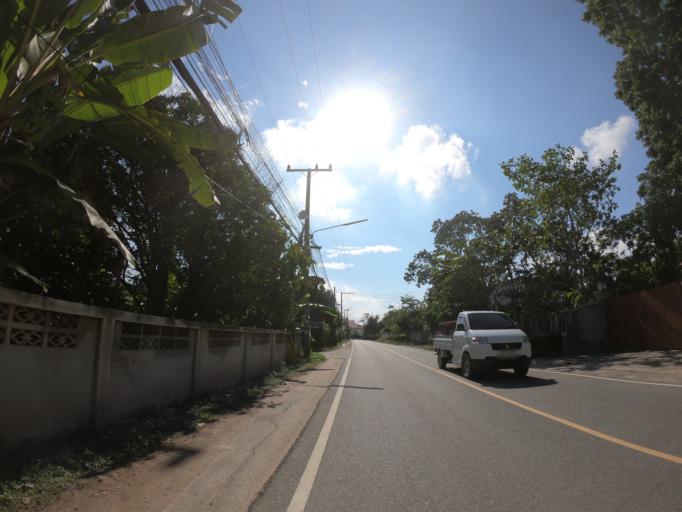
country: TH
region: Chiang Mai
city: San Sai
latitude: 18.8390
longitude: 99.0584
